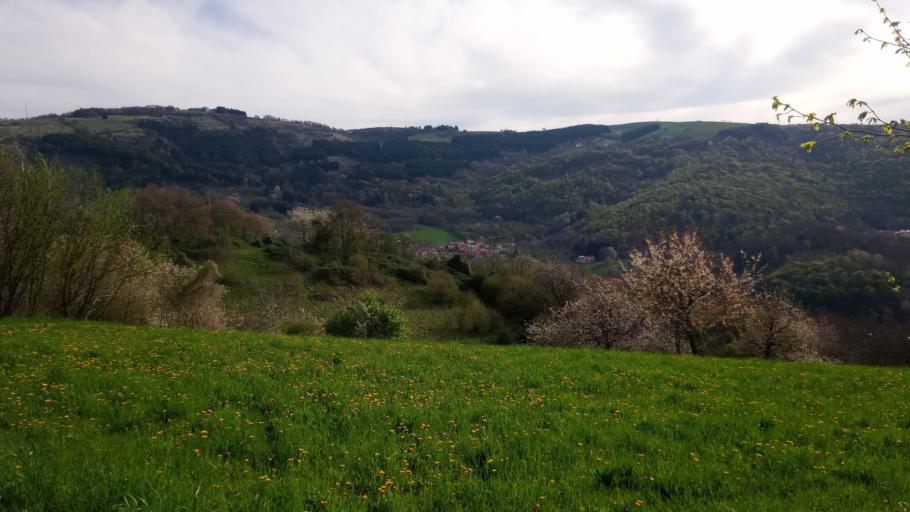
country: IT
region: Veneto
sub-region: Provincia di Vicenza
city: Conco
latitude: 45.7968
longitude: 11.6246
